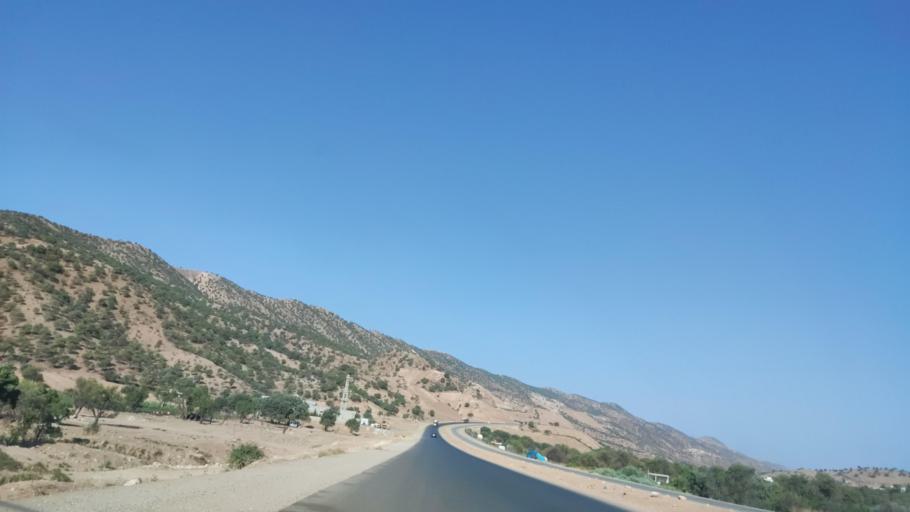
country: IQ
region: Arbil
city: Shaqlawah
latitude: 36.4307
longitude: 44.3199
